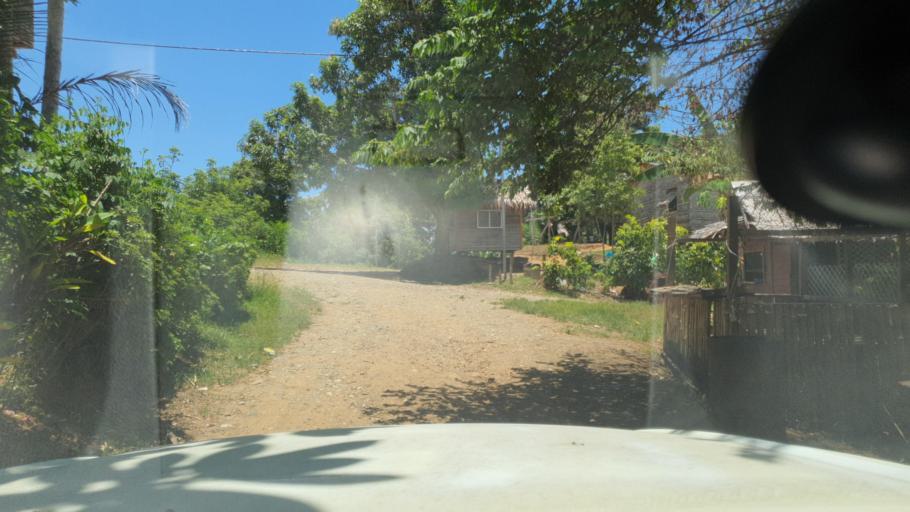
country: SB
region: Guadalcanal
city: Honiara
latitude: -9.4534
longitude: 159.9958
